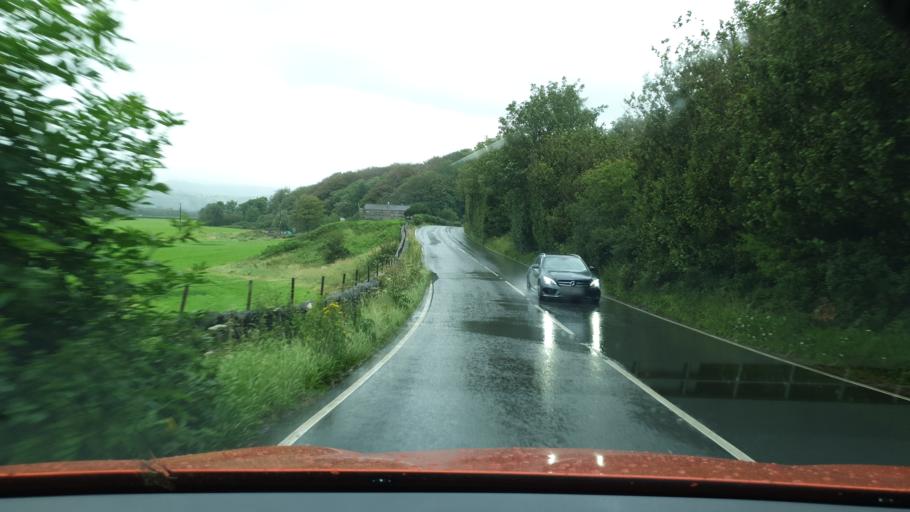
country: GB
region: England
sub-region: Cumbria
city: Askam in Furness
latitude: 54.2592
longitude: -3.1811
